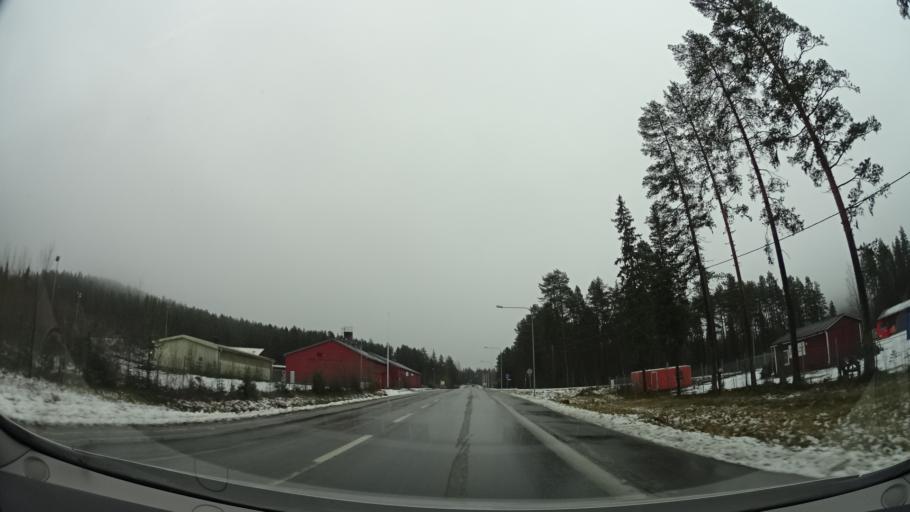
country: SE
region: Vaesterbotten
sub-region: Dorotea Kommun
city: Dorotea
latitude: 64.2589
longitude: 16.3828
